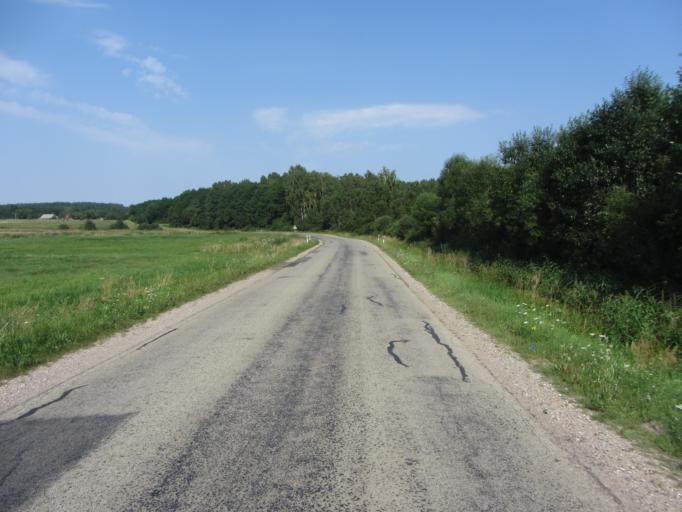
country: LT
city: Veisiejai
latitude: 54.2013
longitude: 23.7682
